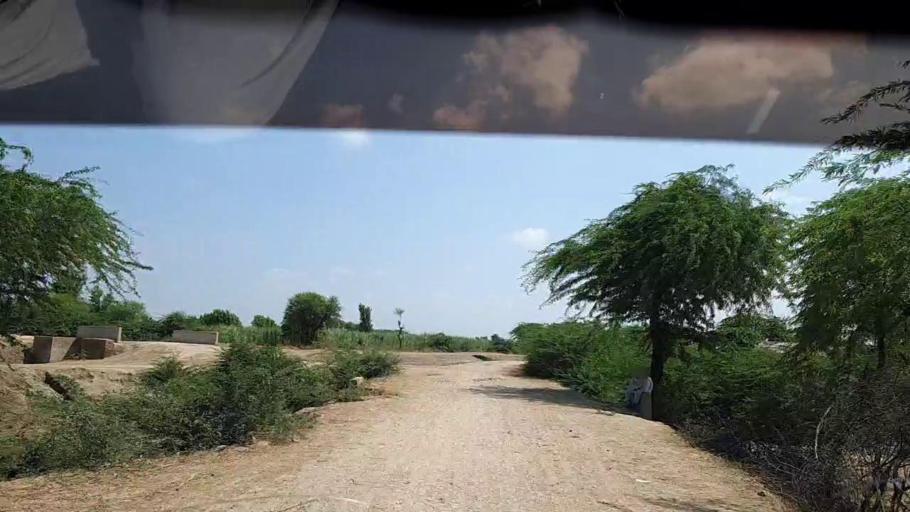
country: PK
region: Sindh
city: Kadhan
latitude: 24.5981
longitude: 68.9912
